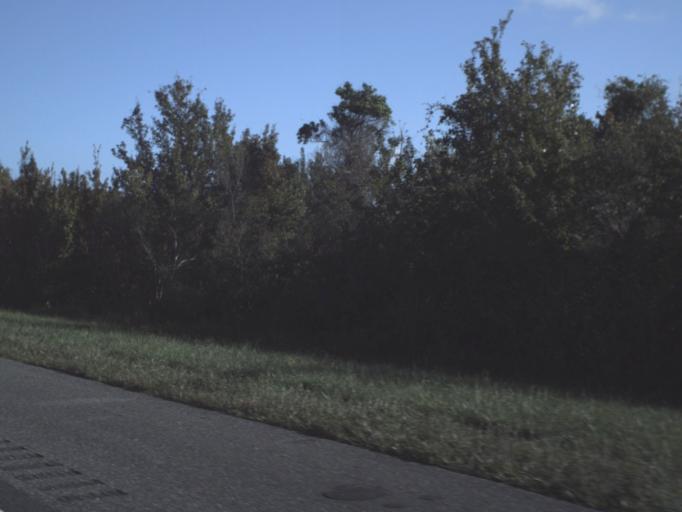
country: US
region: Florida
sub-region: Brevard County
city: June Park
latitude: 27.8352
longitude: -81.0054
